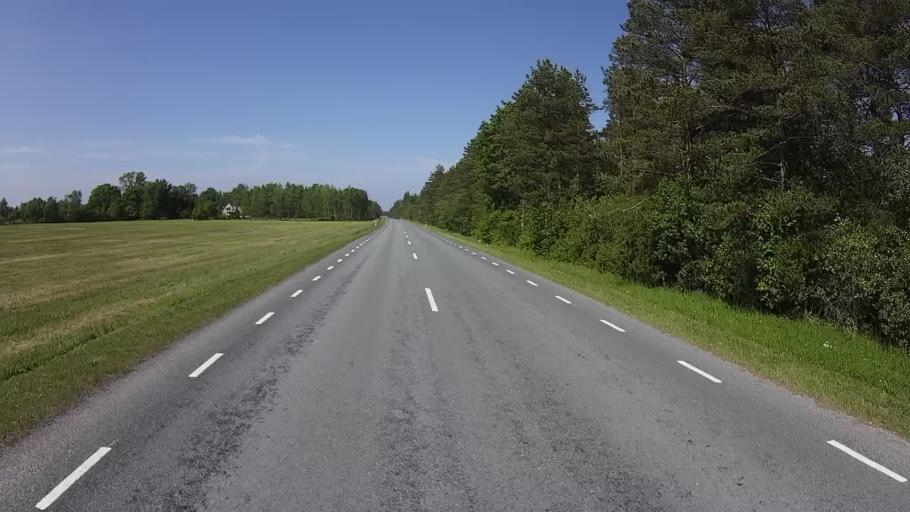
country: EE
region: Saare
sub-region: Kuressaare linn
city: Kuressaare
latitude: 58.3595
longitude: 22.4411
